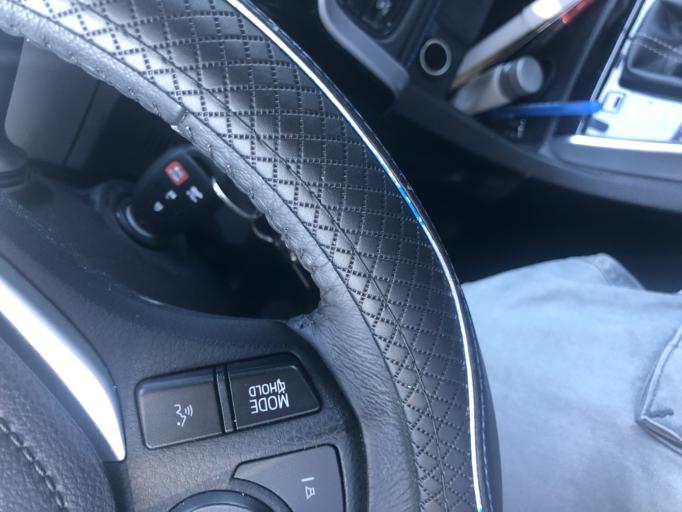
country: US
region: Texas
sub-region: Travis County
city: Wells Branch
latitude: 30.4151
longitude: -97.6649
